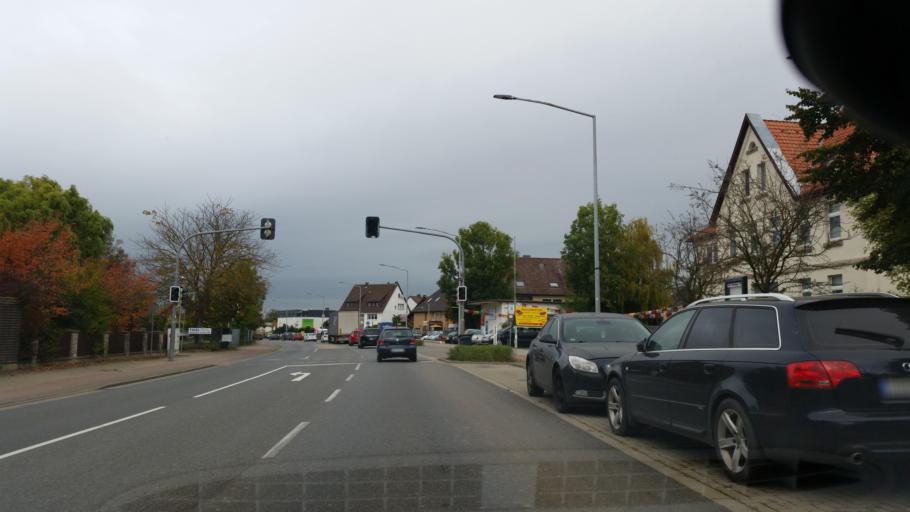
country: DE
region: Lower Saxony
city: Giesen
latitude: 52.1977
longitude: 9.9202
